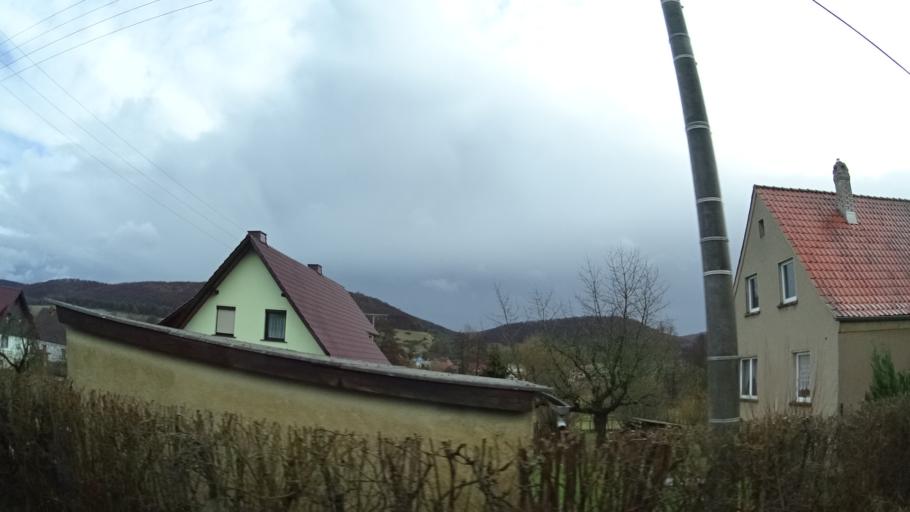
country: DE
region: Thuringia
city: Rippershausen
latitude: 50.5757
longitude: 10.3281
